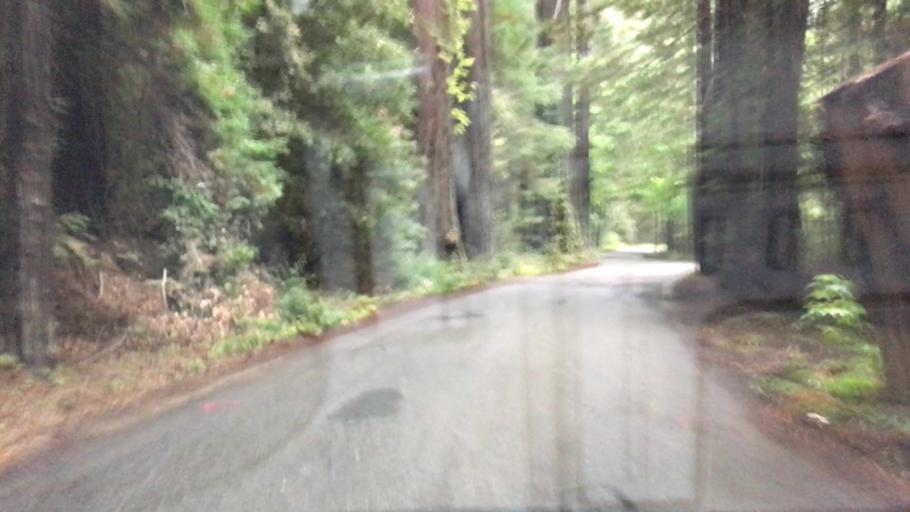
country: US
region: California
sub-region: Humboldt County
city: Rio Dell
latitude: 40.3524
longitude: -123.9815
